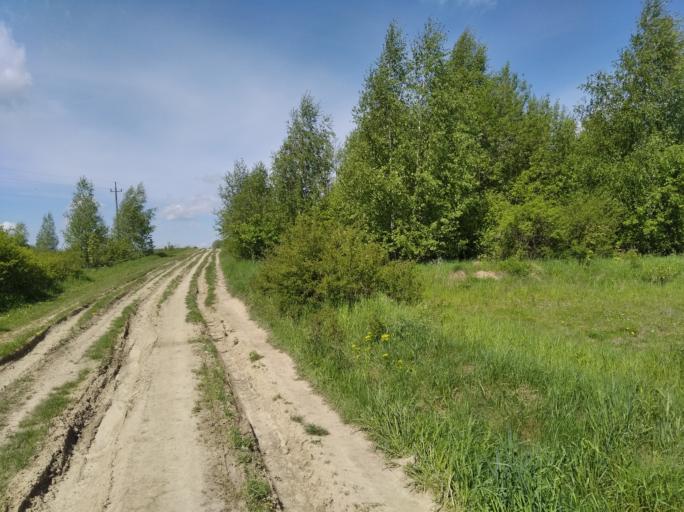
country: PL
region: Subcarpathian Voivodeship
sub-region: Powiat strzyzowski
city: Frysztak
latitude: 49.8336
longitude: 21.5397
